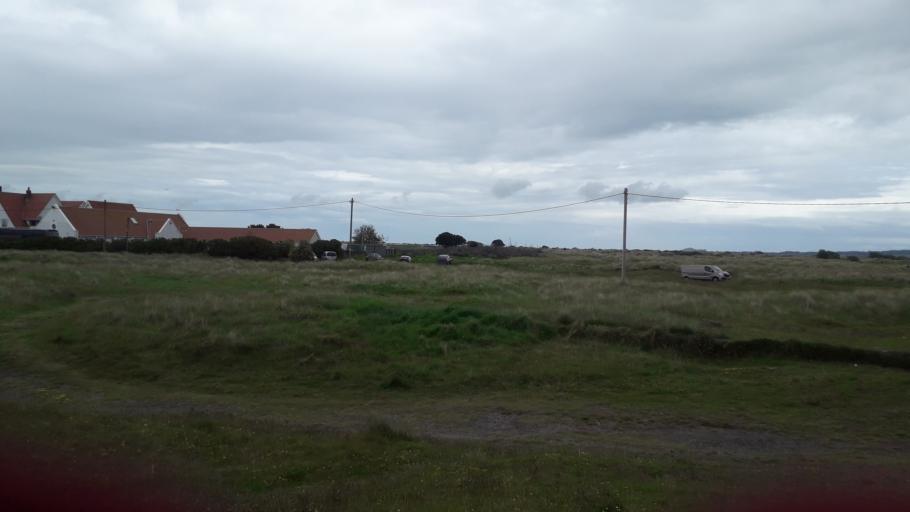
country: IE
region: Leinster
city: Dollymount
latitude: 53.3552
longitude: -6.1708
